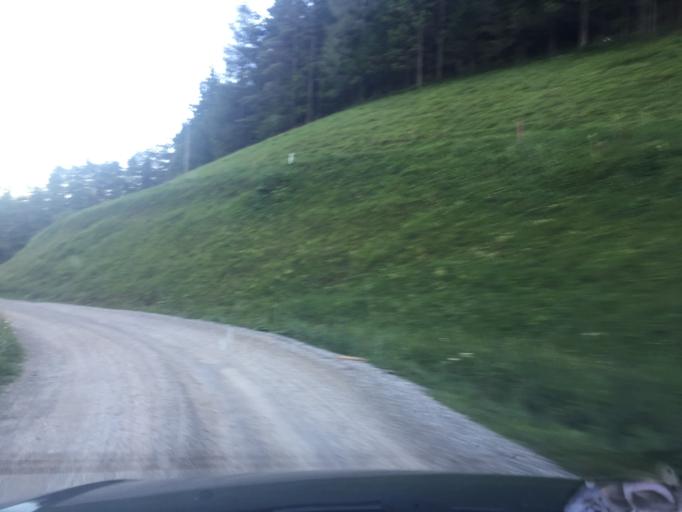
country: SI
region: Ravne na Koroskem
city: Kotlje
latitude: 46.4623
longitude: 14.9934
